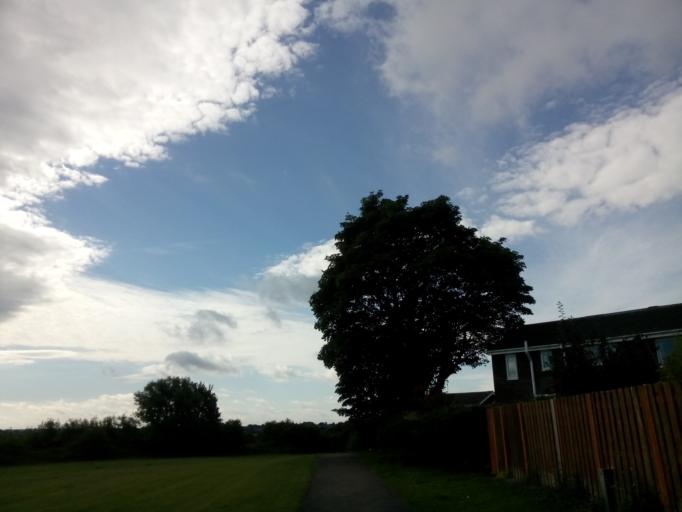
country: GB
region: England
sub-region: County Durham
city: Durham
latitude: 54.7983
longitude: -1.5636
